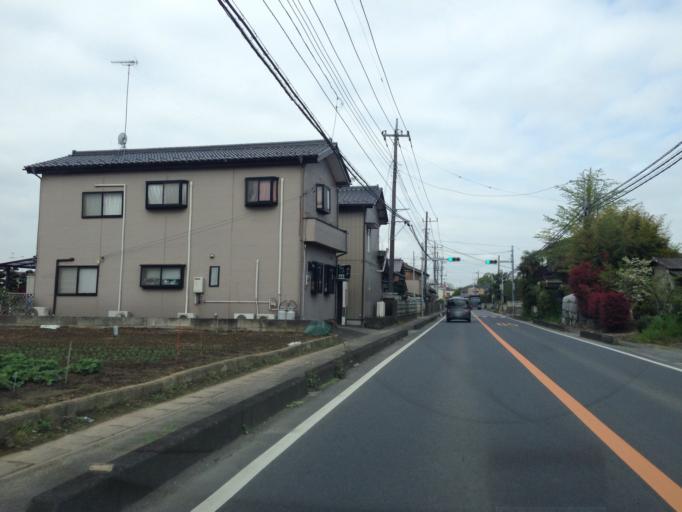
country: JP
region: Ibaraki
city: Ishige
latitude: 36.1551
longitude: 139.9734
